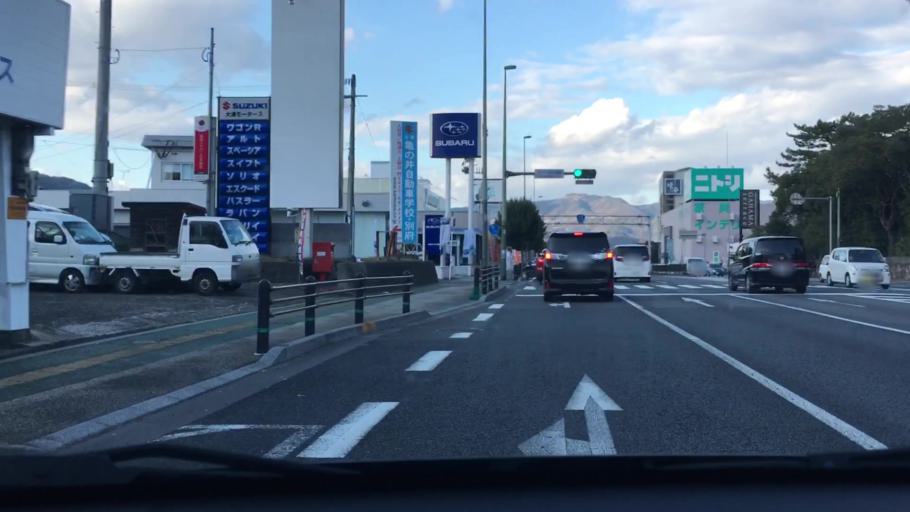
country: JP
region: Oita
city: Beppu
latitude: 33.3145
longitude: 131.5004
